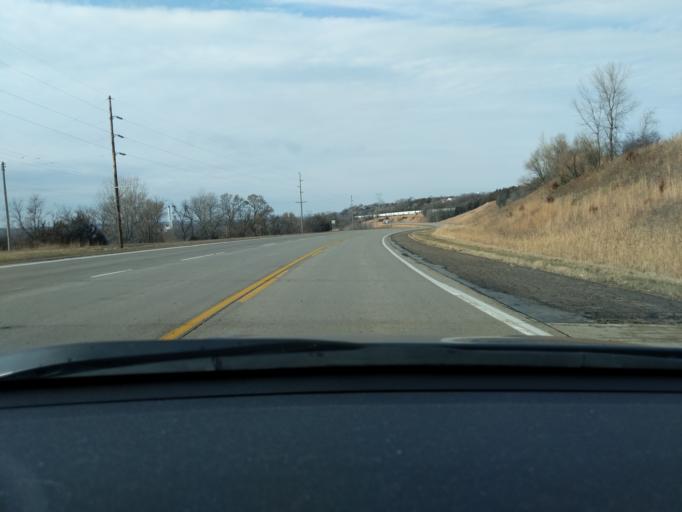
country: US
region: Minnesota
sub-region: Yellow Medicine County
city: Granite Falls
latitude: 44.7977
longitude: -95.5069
